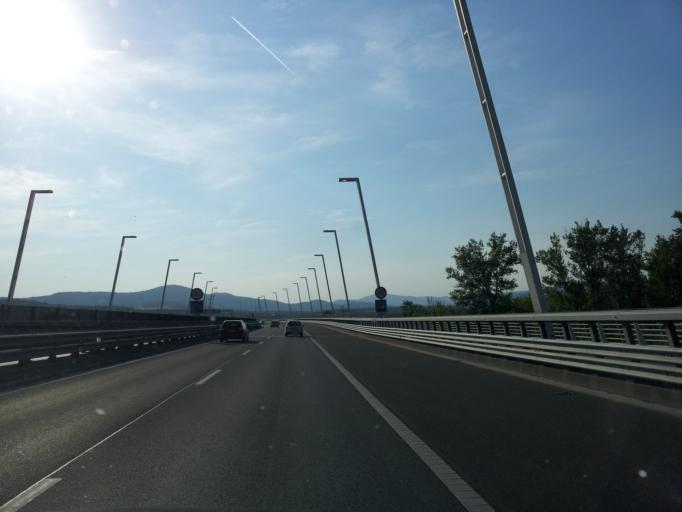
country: HU
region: Pest
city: Budakalasz
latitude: 47.6123
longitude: 19.0794
